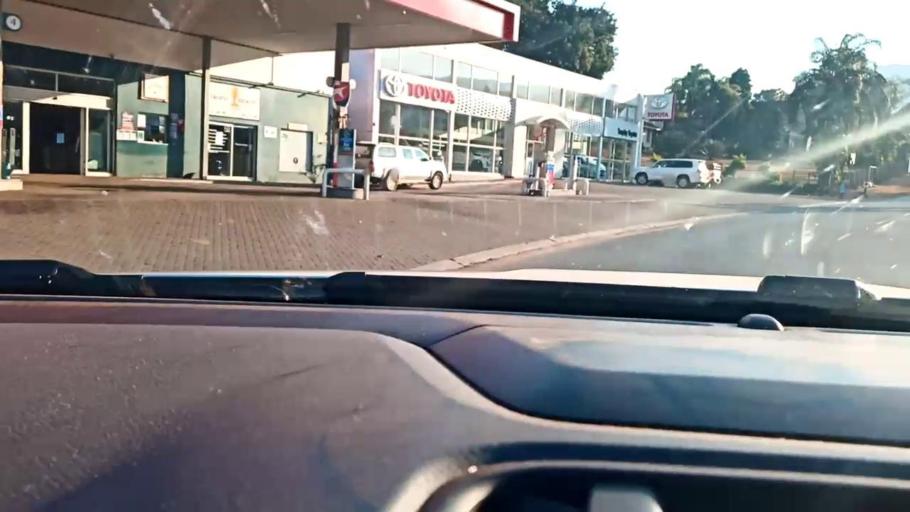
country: ZA
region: Limpopo
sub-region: Mopani District Municipality
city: Duiwelskloof
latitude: -23.6948
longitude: 30.1465
